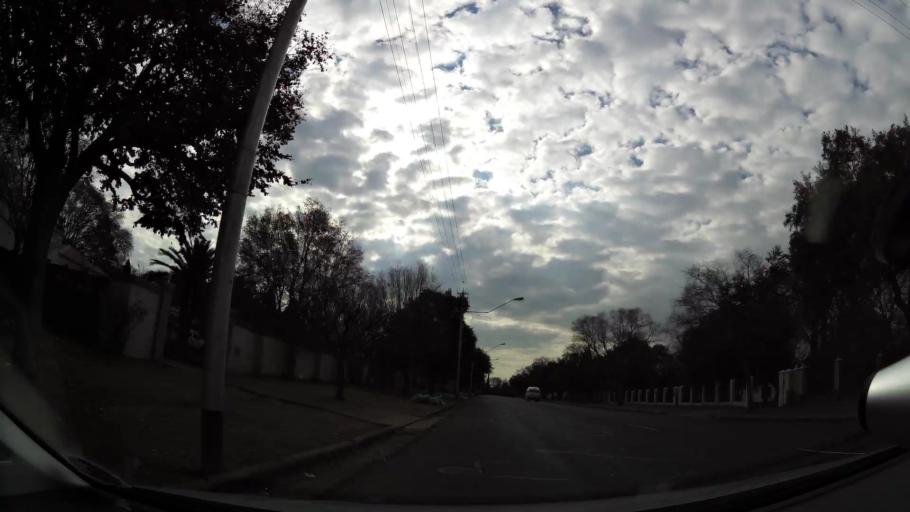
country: ZA
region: Orange Free State
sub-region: Mangaung Metropolitan Municipality
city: Bloemfontein
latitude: -29.0944
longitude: 26.2449
